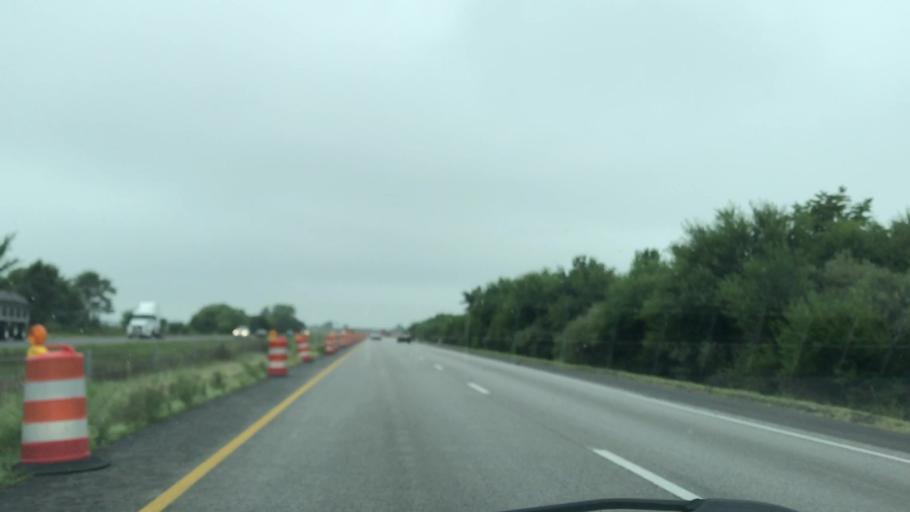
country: US
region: Indiana
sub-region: Clinton County
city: Mulberry
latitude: 40.2525
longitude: -86.6452
